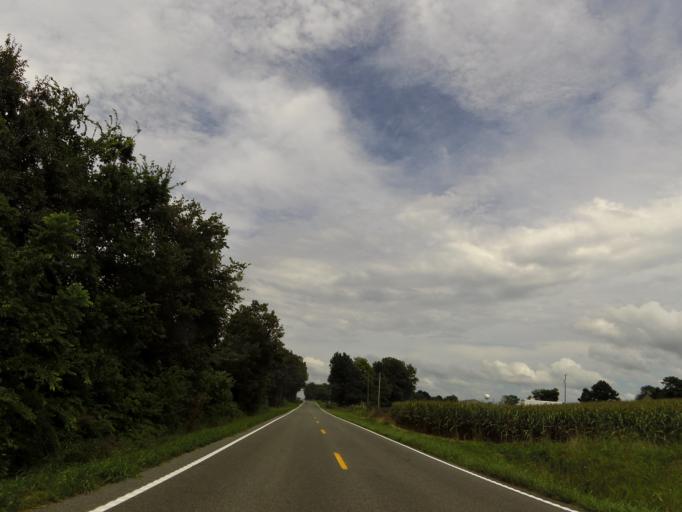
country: US
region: Kentucky
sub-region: McCracken County
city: Massac
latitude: 37.0089
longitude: -88.8253
